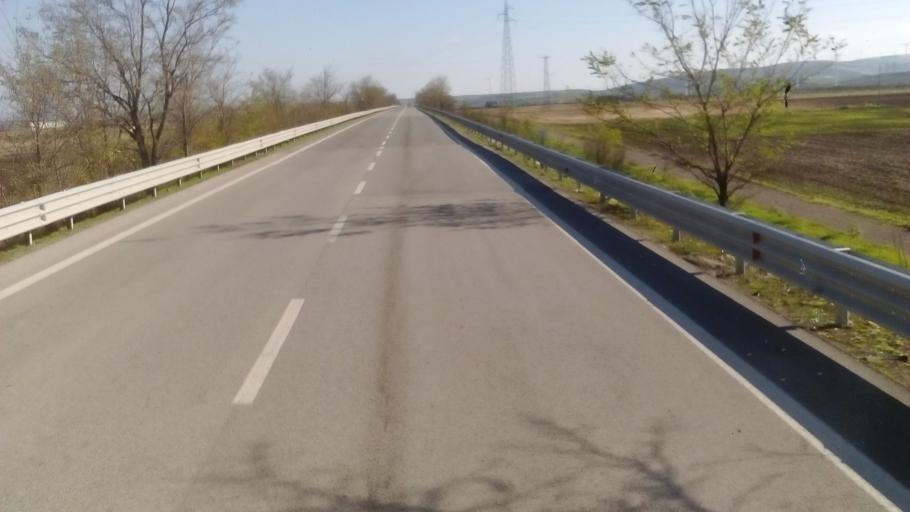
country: IT
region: Basilicate
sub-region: Provincia di Potenza
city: Zona 179
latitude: 41.0786
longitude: 15.6338
